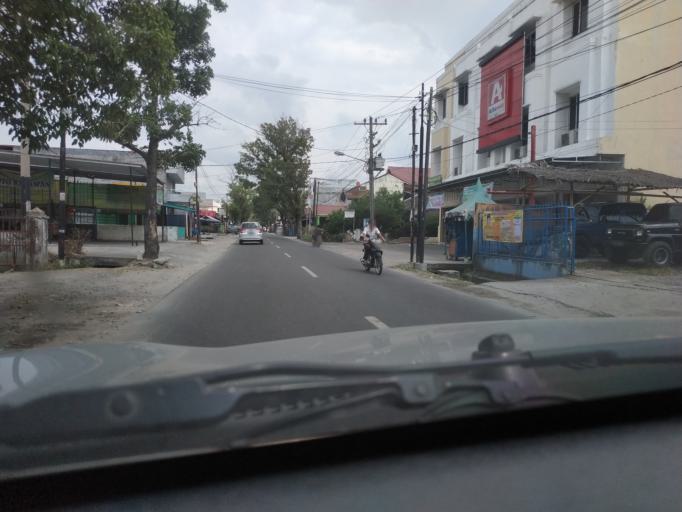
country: ID
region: North Sumatra
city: Sunggal
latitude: 3.5846
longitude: 98.6314
